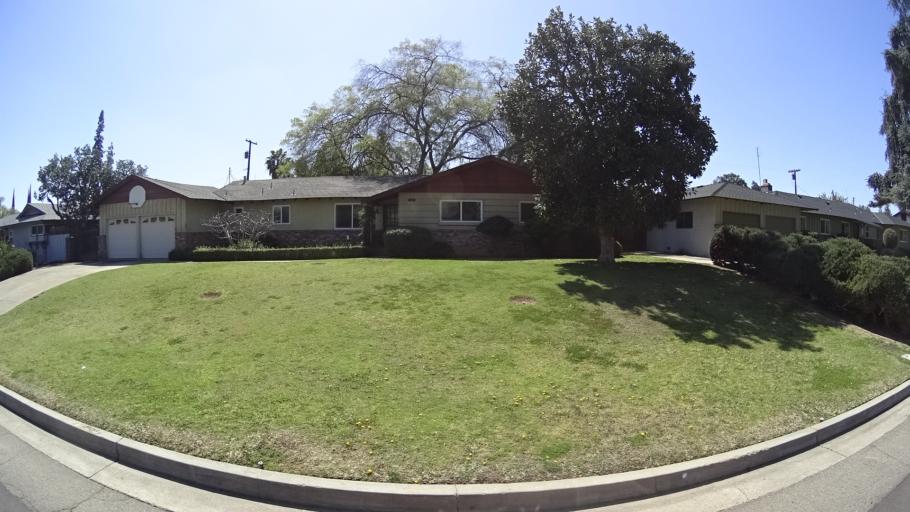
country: US
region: California
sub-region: Fresno County
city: Fresno
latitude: 36.8094
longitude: -119.7941
